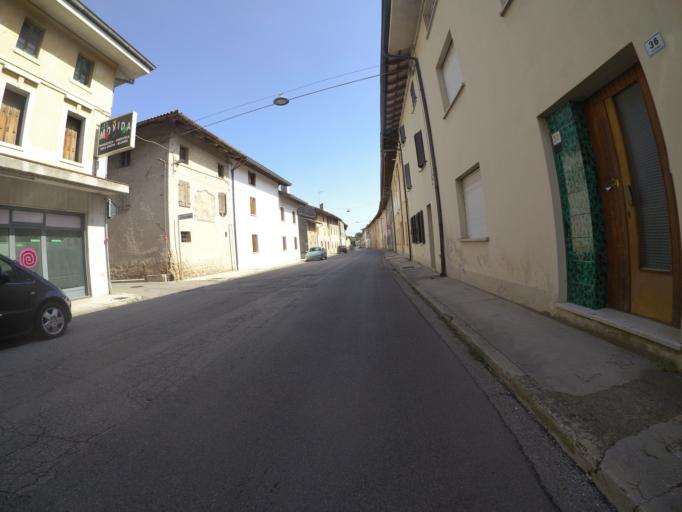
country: IT
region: Friuli Venezia Giulia
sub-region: Provincia di Udine
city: Mortegliano
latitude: 45.9415
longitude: 13.1722
